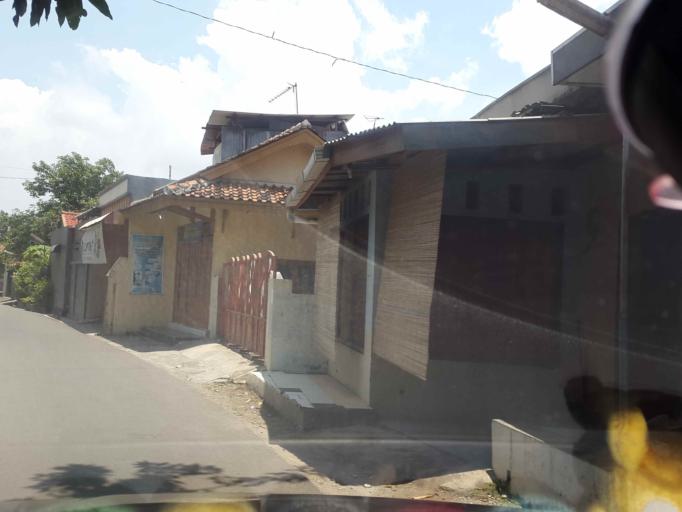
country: ID
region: Central Java
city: Tegal
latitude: -6.8733
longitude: 109.1381
